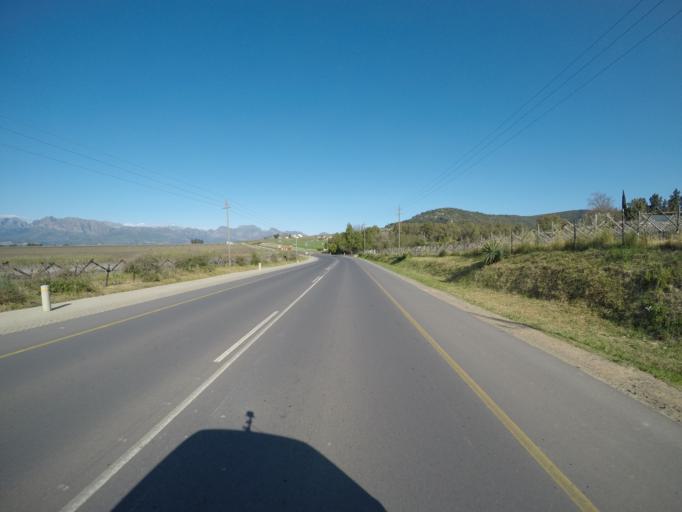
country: ZA
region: Western Cape
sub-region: Cape Winelands District Municipality
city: Noorder-Paarl
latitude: -33.6747
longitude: 18.9335
